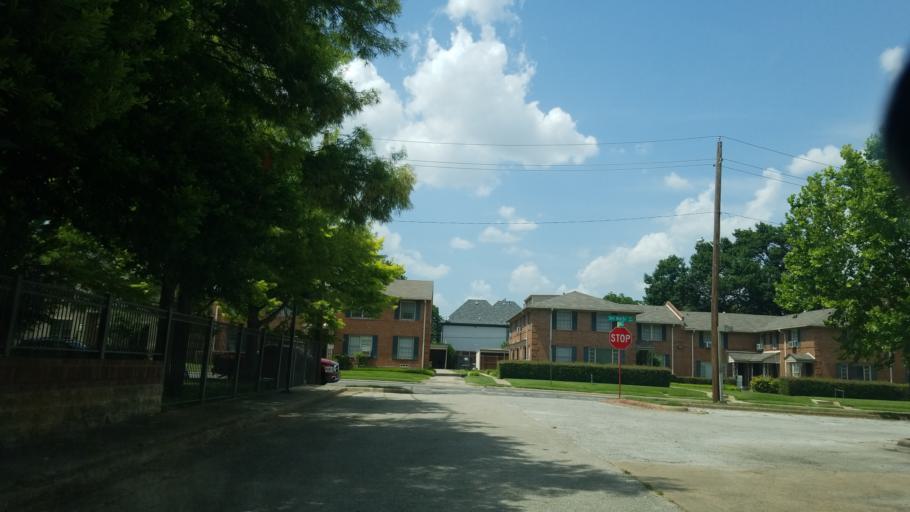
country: US
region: Texas
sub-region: Dallas County
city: University Park
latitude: 32.8683
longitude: -96.7876
